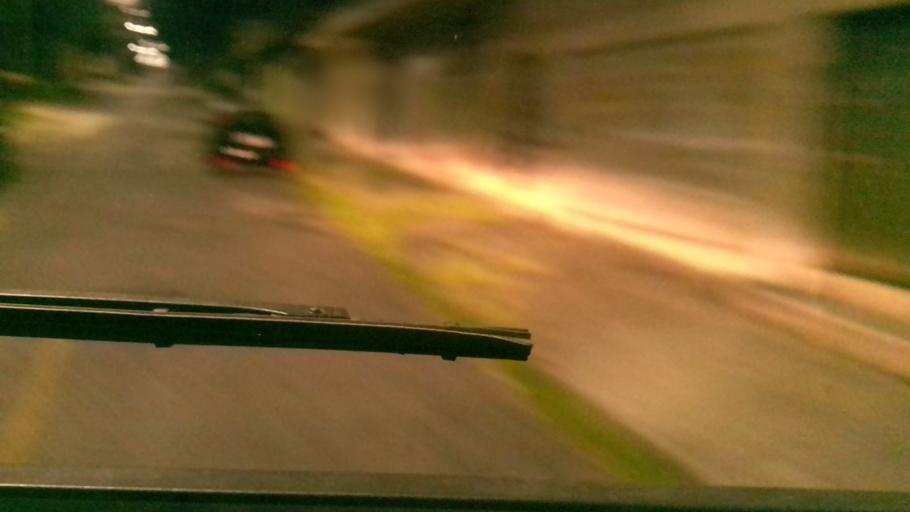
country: BR
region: Minas Gerais
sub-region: Belo Horizonte
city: Belo Horizonte
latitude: -19.8630
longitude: -43.9194
